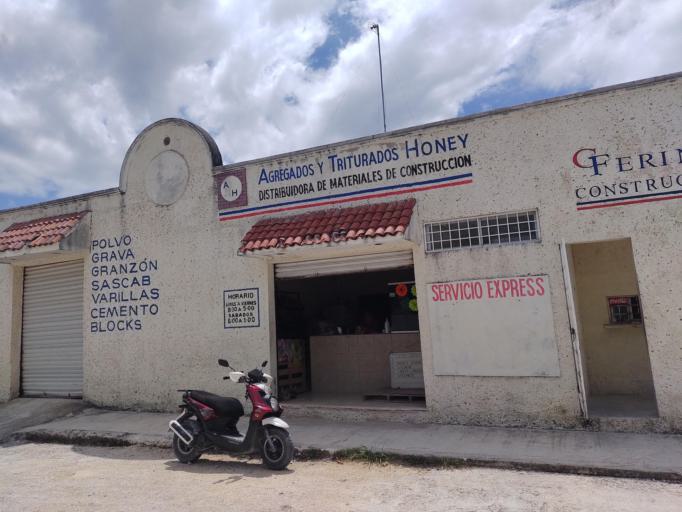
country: MX
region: Quintana Roo
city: San Miguel de Cozumel
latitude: 20.4880
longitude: -86.9092
